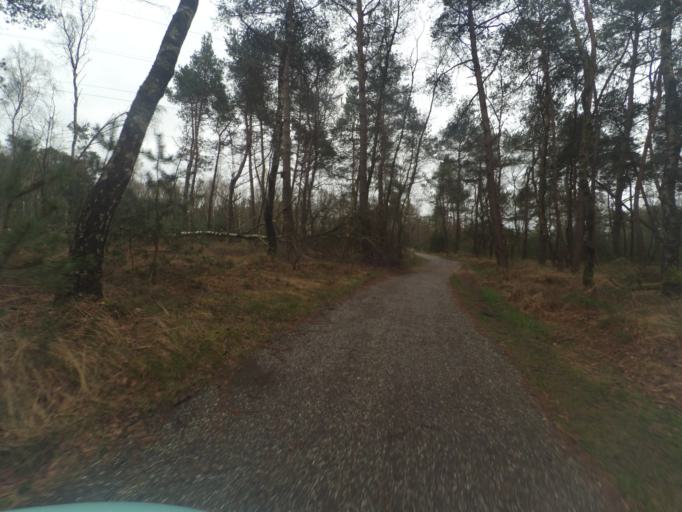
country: NL
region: Gelderland
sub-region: Gemeente Arnhem
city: Gulden Bodem
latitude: 52.0230
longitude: 5.9106
